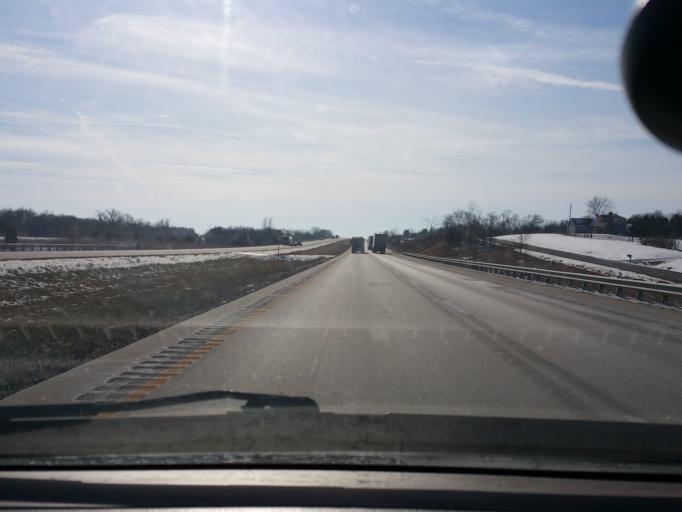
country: US
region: Missouri
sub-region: Clinton County
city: Cameron
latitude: 39.6579
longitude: -94.2383
